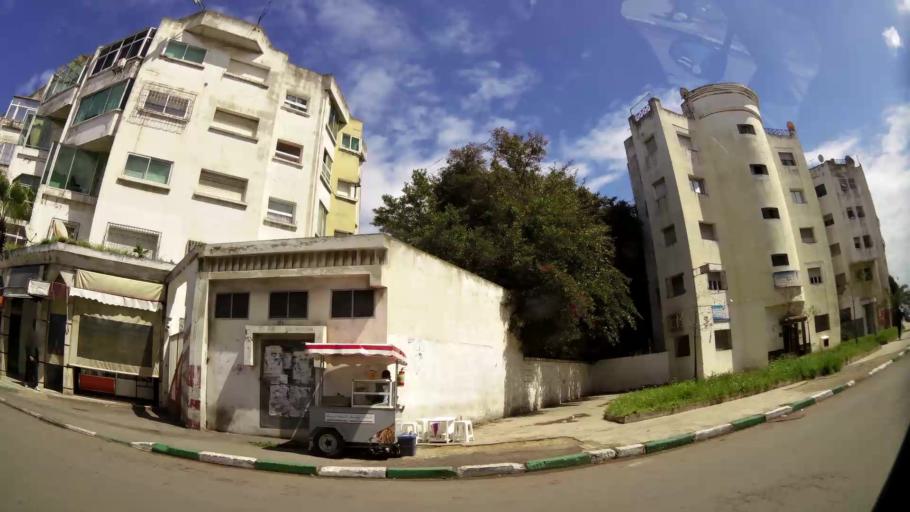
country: MA
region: Grand Casablanca
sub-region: Mediouna
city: Tit Mellil
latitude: 33.5989
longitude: -7.5198
